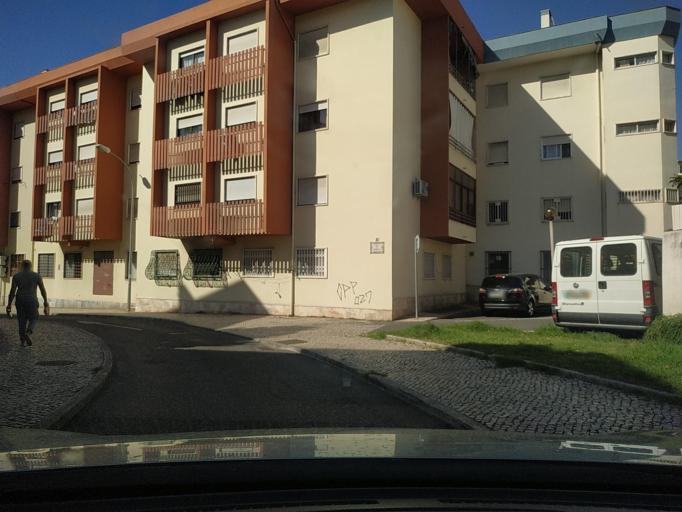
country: PT
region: Lisbon
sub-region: Sintra
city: Queluz
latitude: 38.7595
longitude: -9.2449
